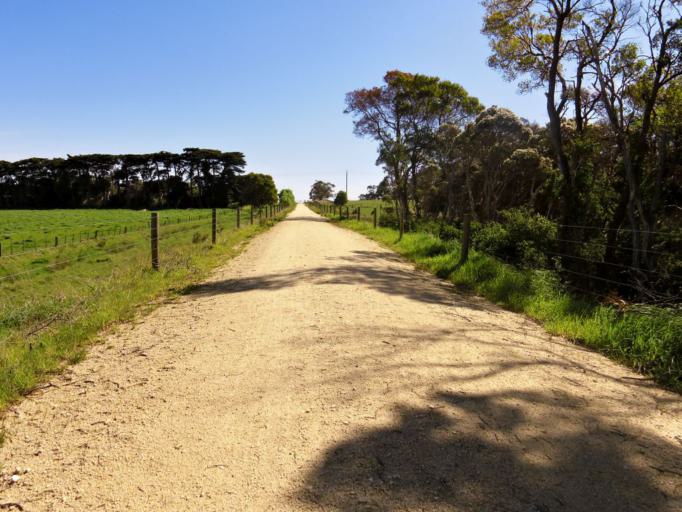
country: AU
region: Victoria
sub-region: Latrobe
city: Morwell
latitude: -38.6684
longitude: 146.3393
